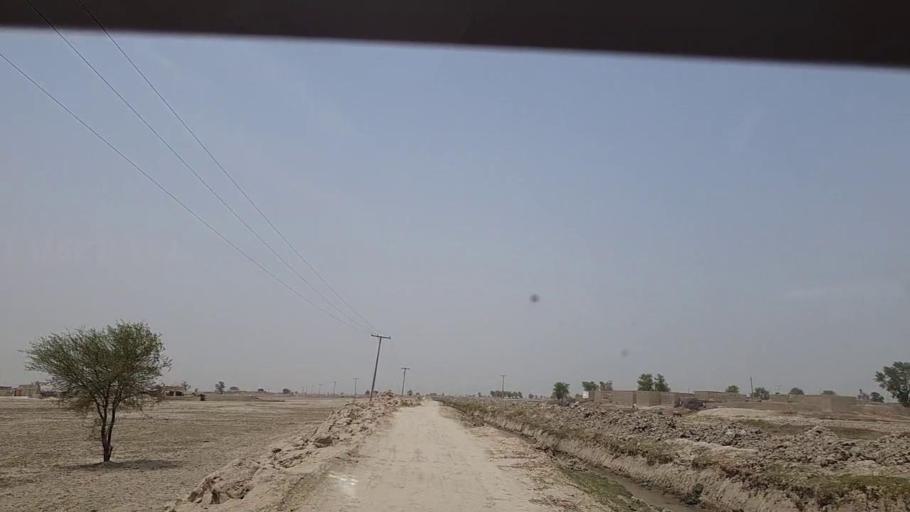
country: PK
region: Sindh
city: Khairpur Nathan Shah
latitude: 27.0538
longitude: 67.6193
